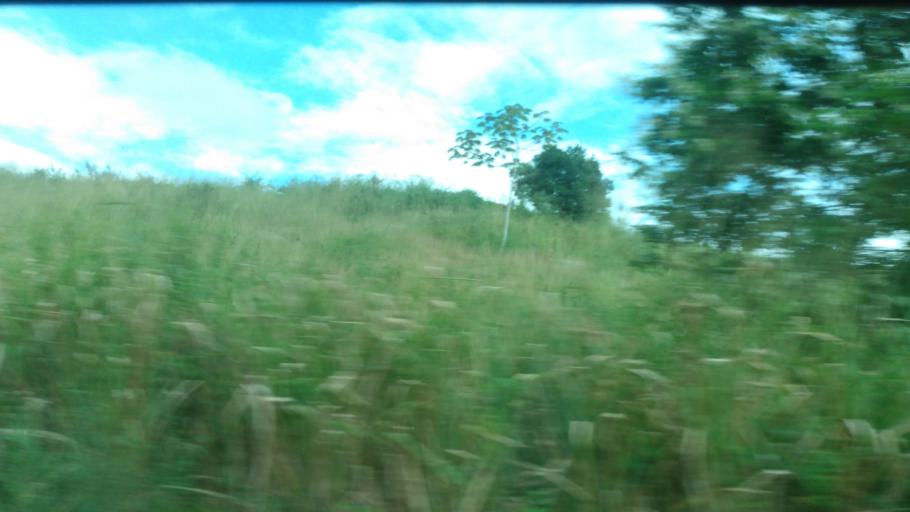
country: BR
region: Pernambuco
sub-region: Catende
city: Catende
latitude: -8.6942
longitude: -35.7273
